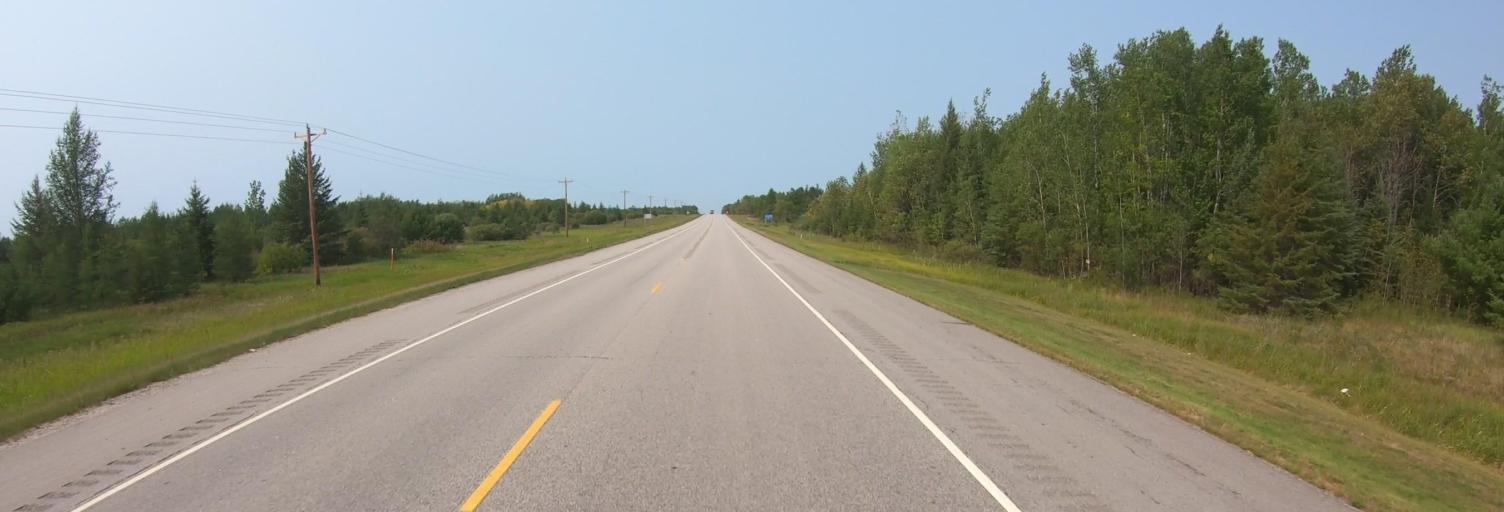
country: CA
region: Ontario
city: Fort Frances
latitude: 48.4101
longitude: -93.1512
